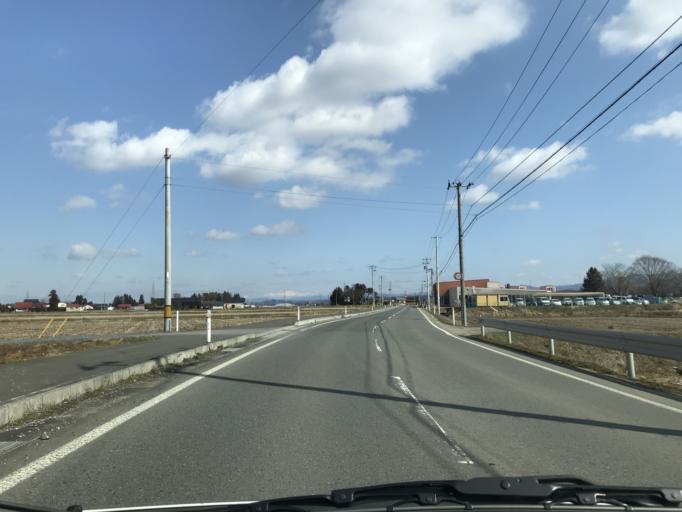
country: JP
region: Iwate
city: Mizusawa
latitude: 39.0714
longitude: 141.1472
